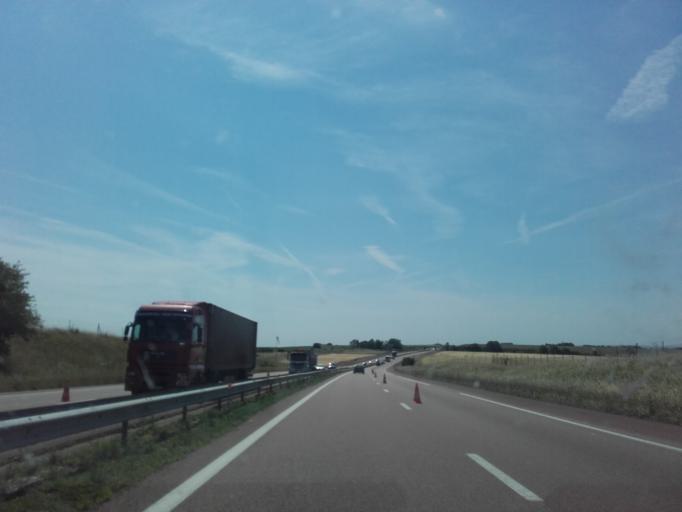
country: FR
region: Bourgogne
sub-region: Departement de l'Yonne
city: Joux-la-Ville
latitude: 47.5776
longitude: 3.9333
